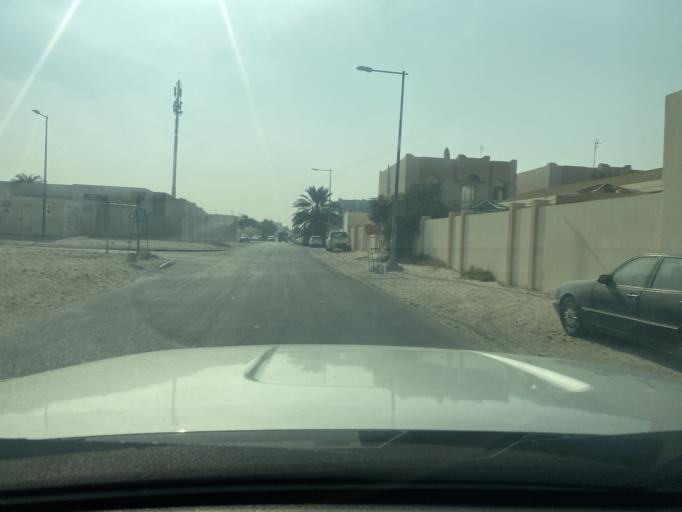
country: QA
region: Baladiyat ad Dawhah
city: Doha
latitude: 25.2378
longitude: 51.5686
